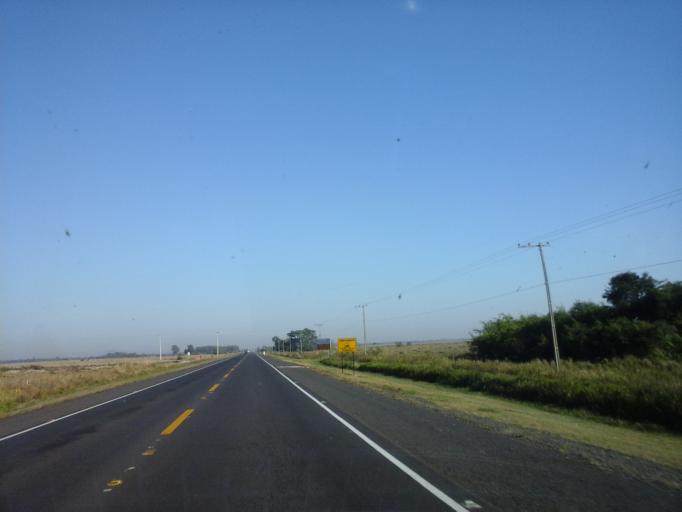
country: PY
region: Neembucu
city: Pilar
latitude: -26.8499
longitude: -58.2291
